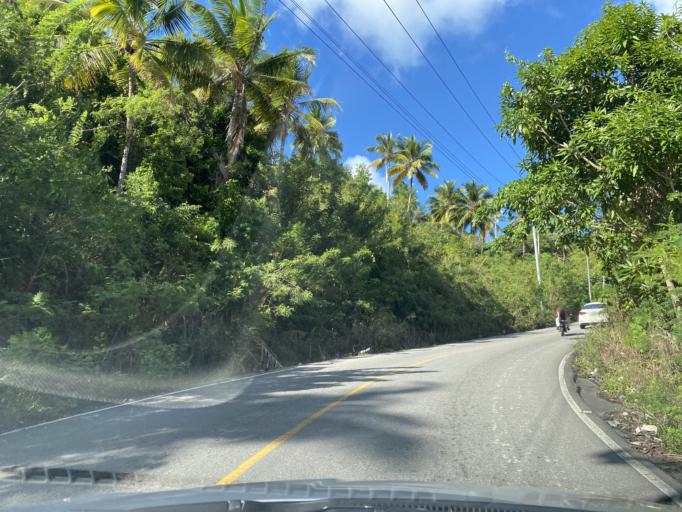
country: DO
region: Samana
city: Sanchez
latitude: 19.2369
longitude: -69.5959
